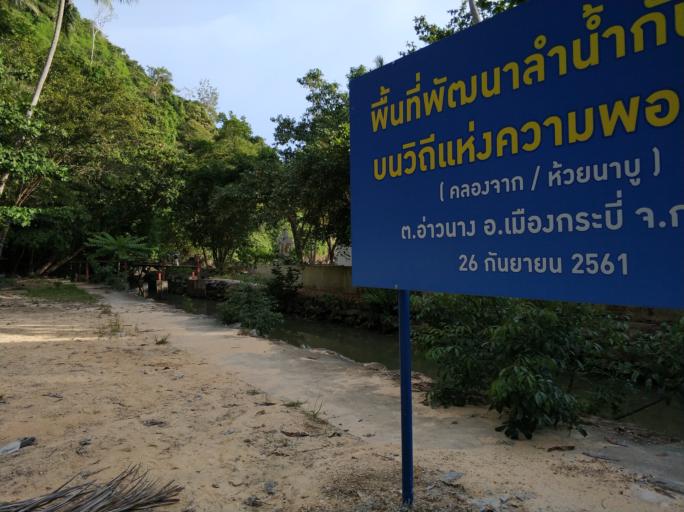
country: TH
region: Phangnga
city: Ban Ao Nang
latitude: 8.0277
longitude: 98.8264
